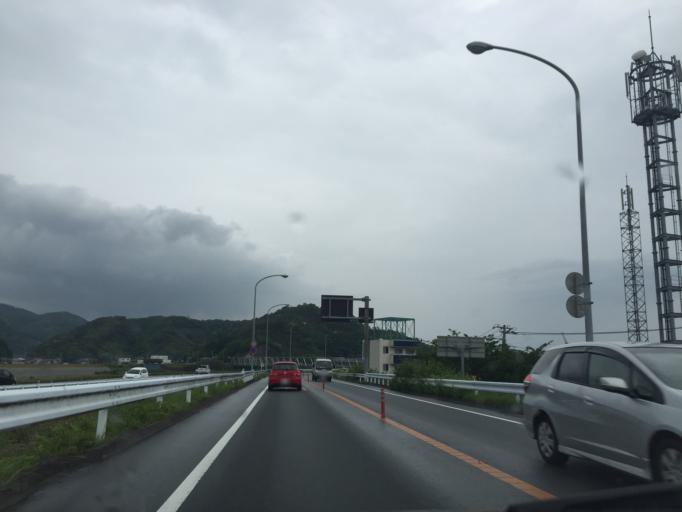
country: JP
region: Shizuoka
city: Mishima
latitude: 35.0163
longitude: 138.9400
